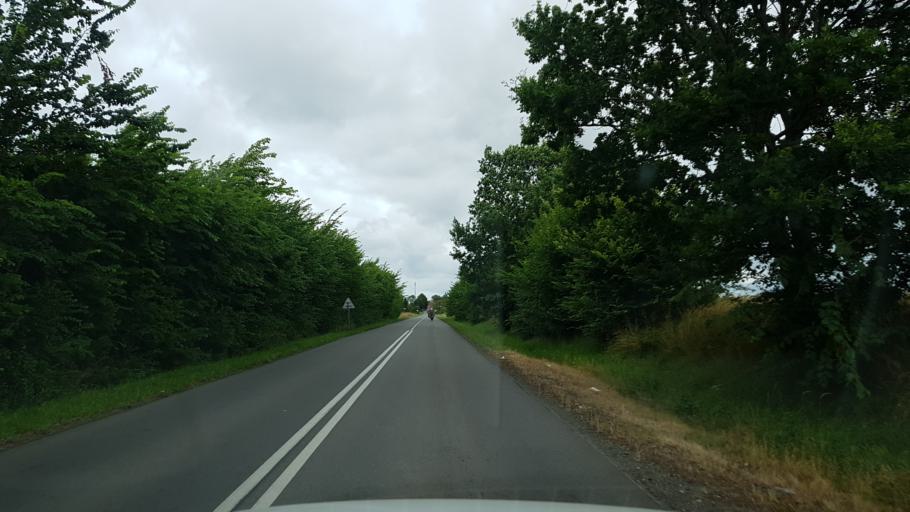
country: PL
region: West Pomeranian Voivodeship
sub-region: Powiat gryficki
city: Rewal
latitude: 54.0662
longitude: 15.0289
